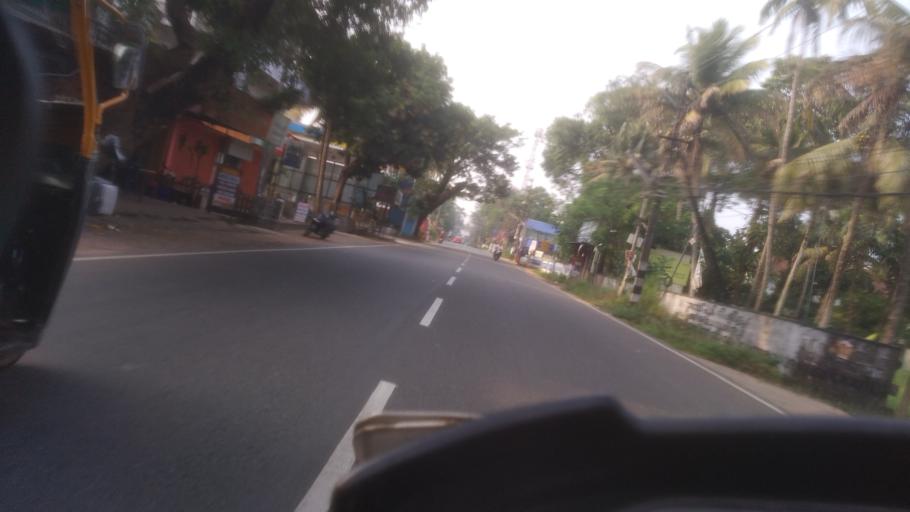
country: IN
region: Kerala
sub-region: Alappuzha
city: Arukutti
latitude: 9.8817
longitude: 76.3757
